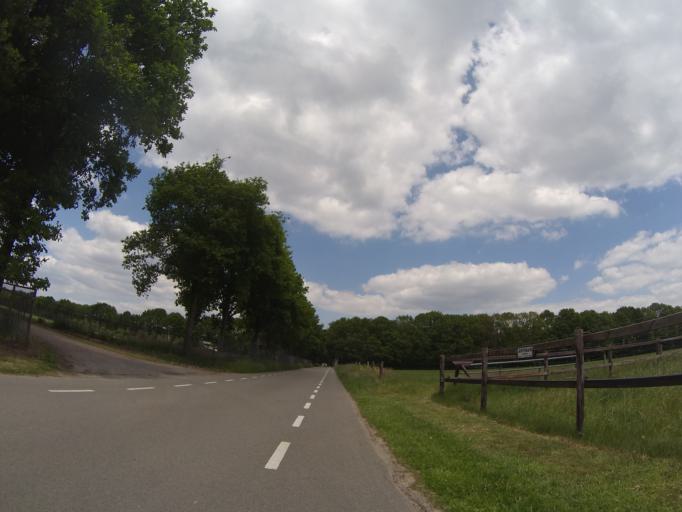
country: NL
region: Gelderland
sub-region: Gemeente Ede
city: Harskamp
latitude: 52.1818
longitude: 5.7675
